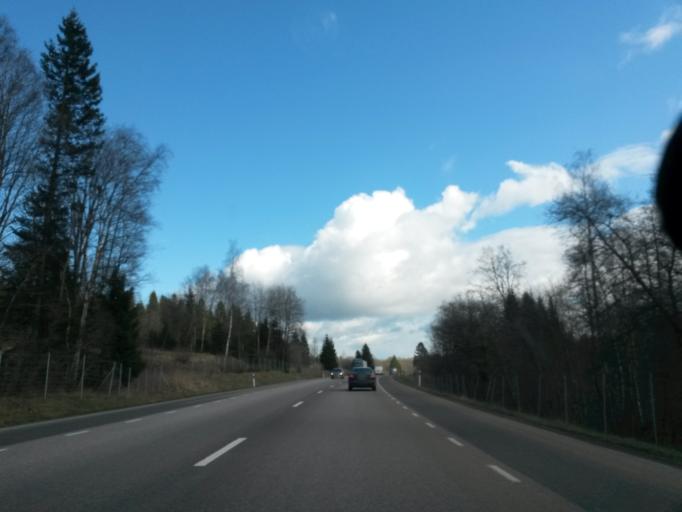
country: SE
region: Vaestra Goetaland
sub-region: Skovde Kommun
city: Skoevde
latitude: 58.3934
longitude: 13.7755
